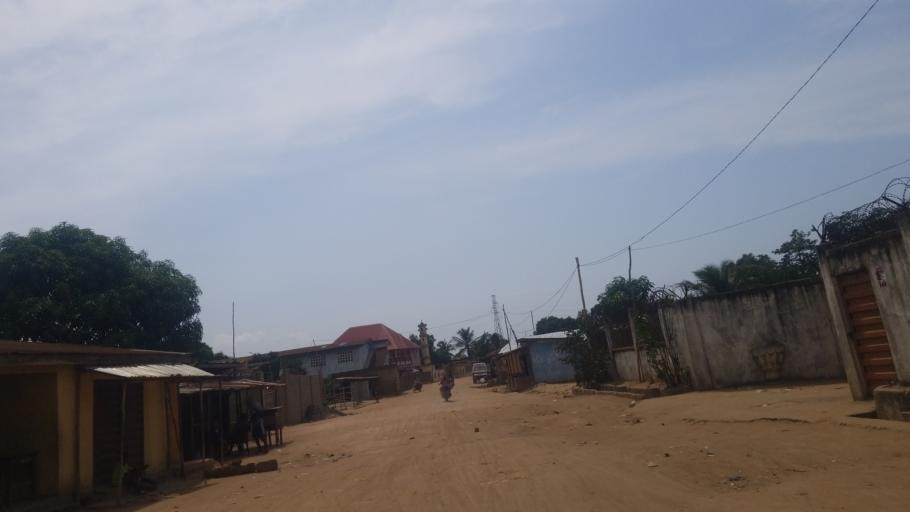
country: SL
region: Western Area
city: Waterloo
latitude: 8.3238
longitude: -13.0470
